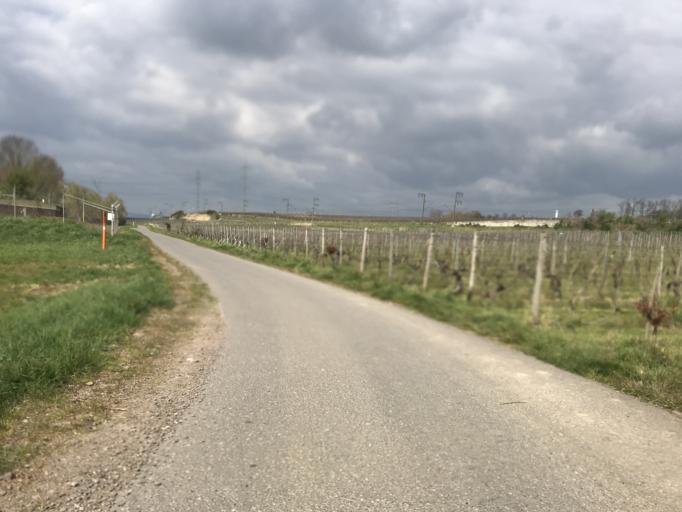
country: DE
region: Hesse
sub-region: Regierungsbezirk Darmstadt
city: Bischofsheim
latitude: 49.9997
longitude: 8.3910
